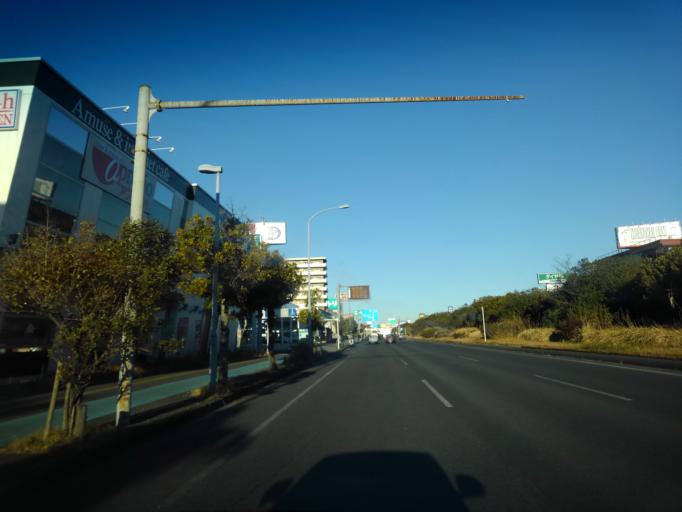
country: JP
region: Chiba
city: Funabashi
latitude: 35.6598
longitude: 140.0477
